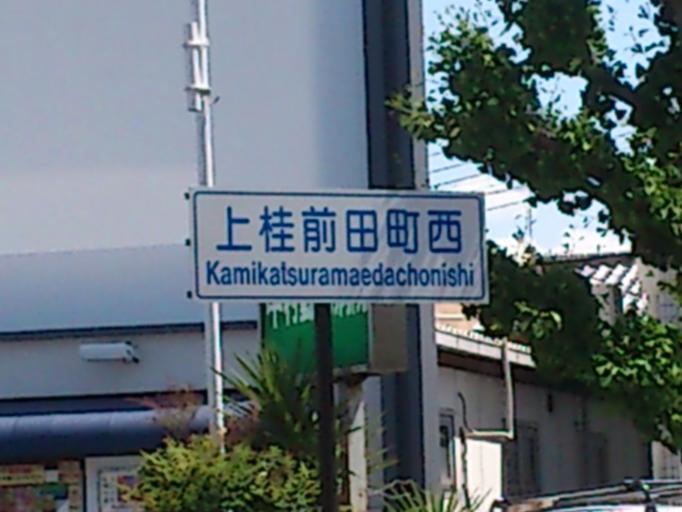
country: JP
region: Kyoto
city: Muko
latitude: 34.9877
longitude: 135.6985
